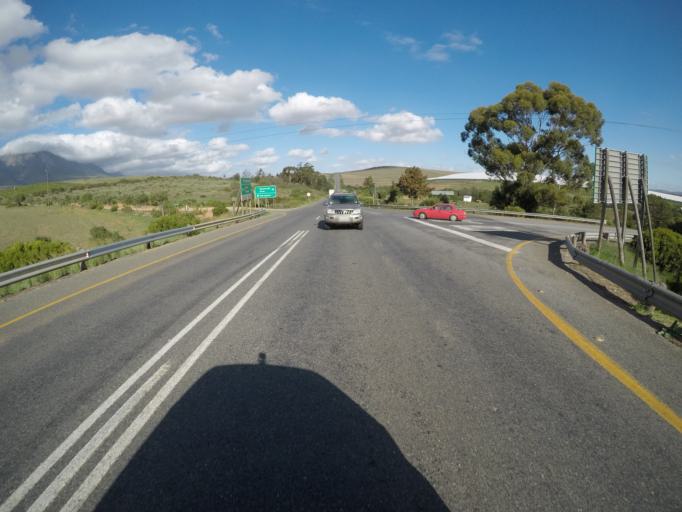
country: ZA
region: Western Cape
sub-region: Overberg District Municipality
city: Swellendam
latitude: -33.9605
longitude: 20.2404
